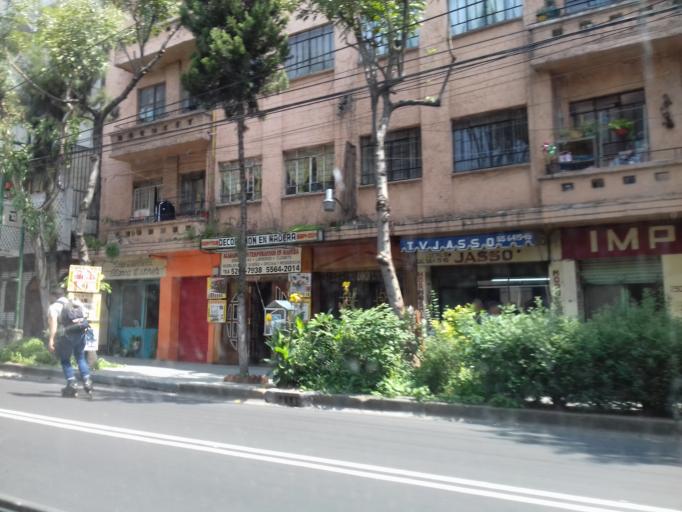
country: MX
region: Mexico City
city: Benito Juarez
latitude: 19.4085
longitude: -99.1618
